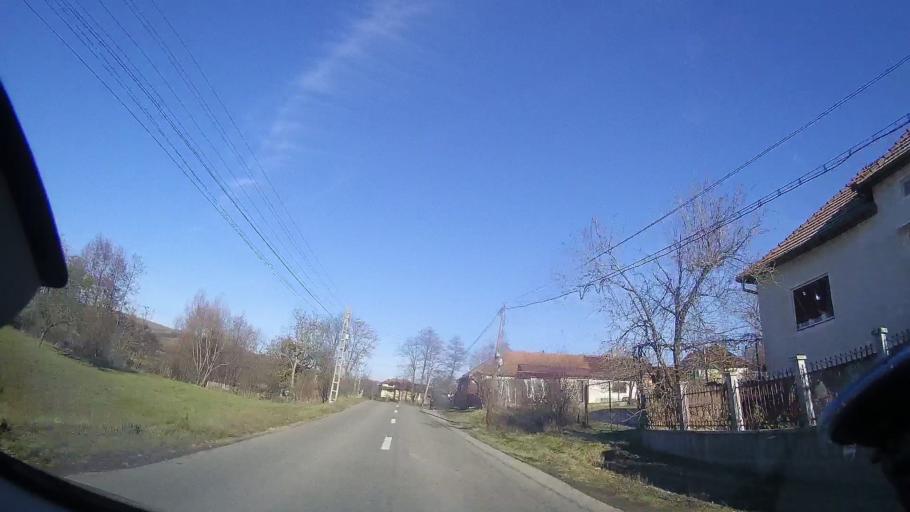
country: RO
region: Bihor
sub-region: Comuna Bratca
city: Bratca
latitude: 46.9401
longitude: 22.6043
